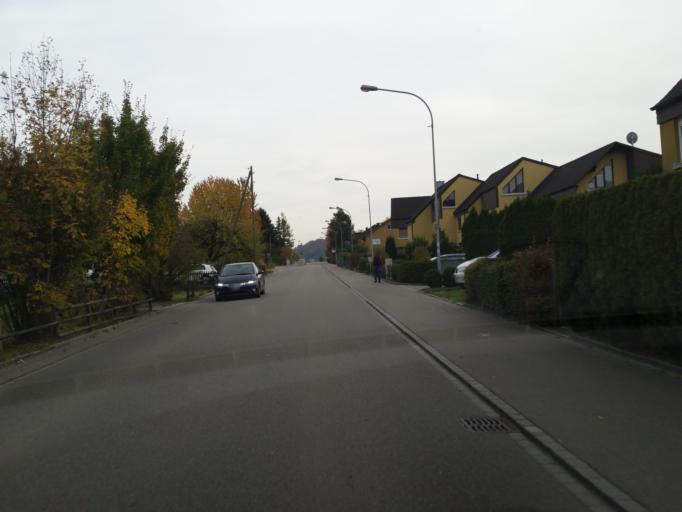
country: CH
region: Zurich
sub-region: Bezirk Winterthur
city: Neftenbach / Dorf Neftenbach
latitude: 47.5234
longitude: 8.6691
